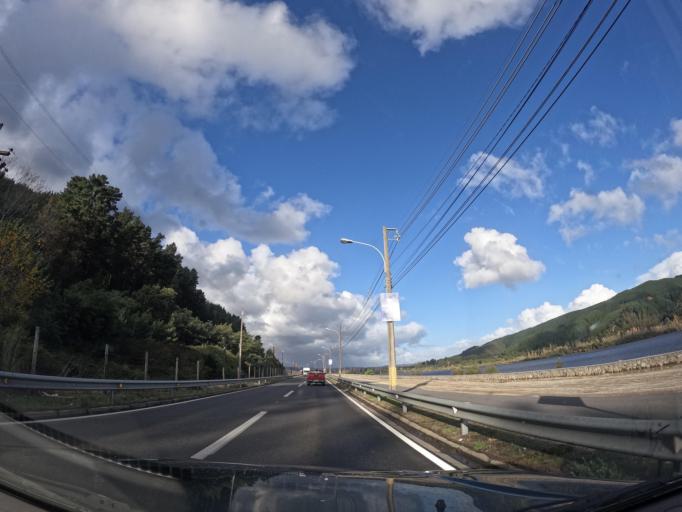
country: CL
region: Biobio
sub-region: Provincia de Concepcion
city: Chiguayante
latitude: -36.9702
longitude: -72.9813
